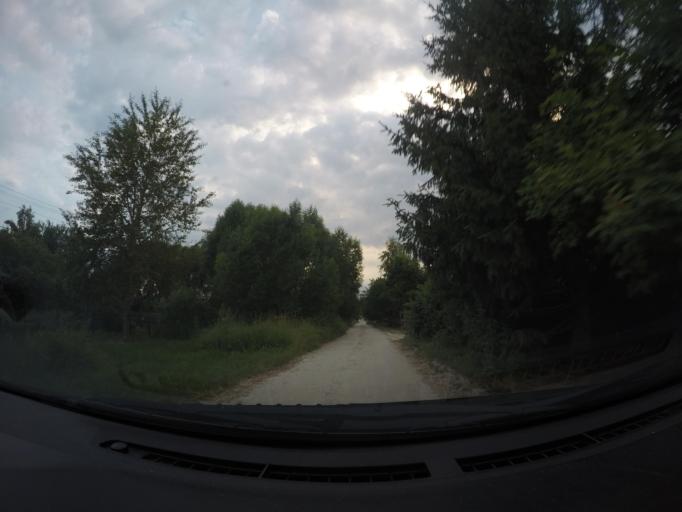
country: RU
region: Moskovskaya
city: Krasnyy Tkach
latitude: 55.3857
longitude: 39.2121
